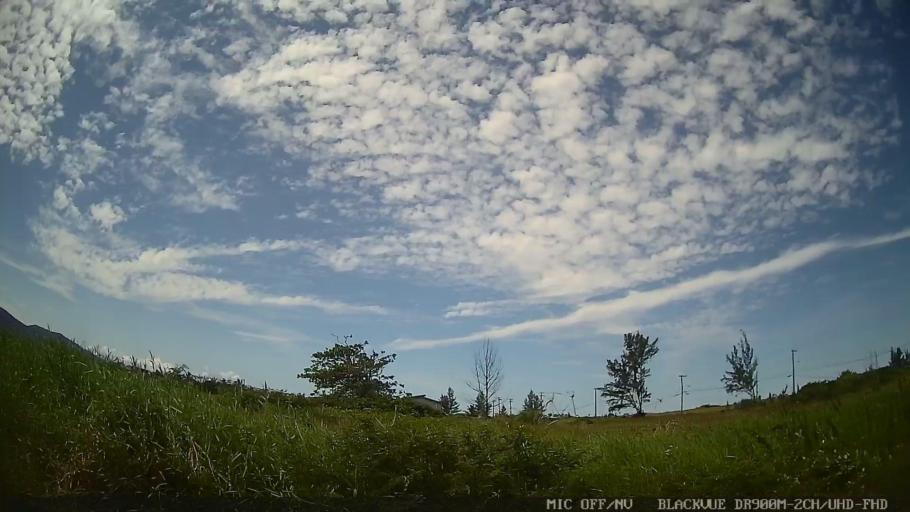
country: BR
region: Sao Paulo
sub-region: Iguape
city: Iguape
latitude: -24.7238
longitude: -47.5082
